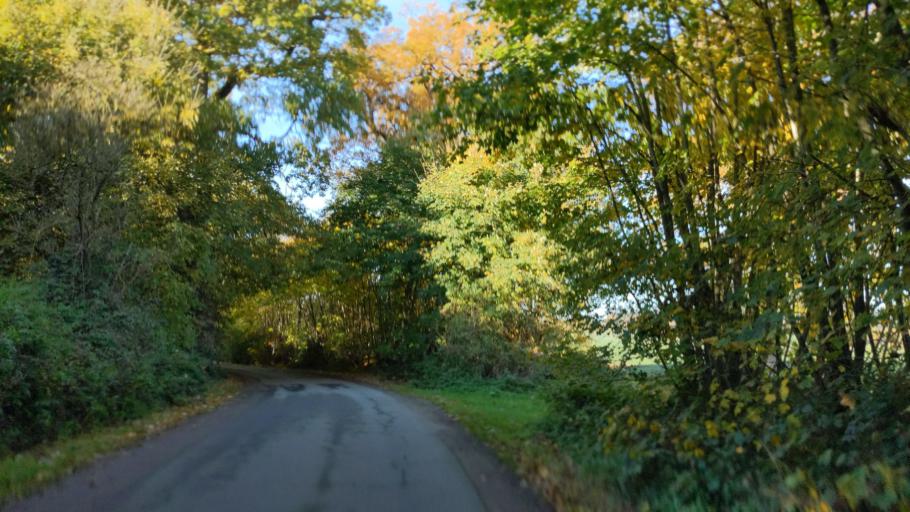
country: DE
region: Schleswig-Holstein
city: Schonwalde am Bungsberg
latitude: 54.1297
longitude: 10.7589
